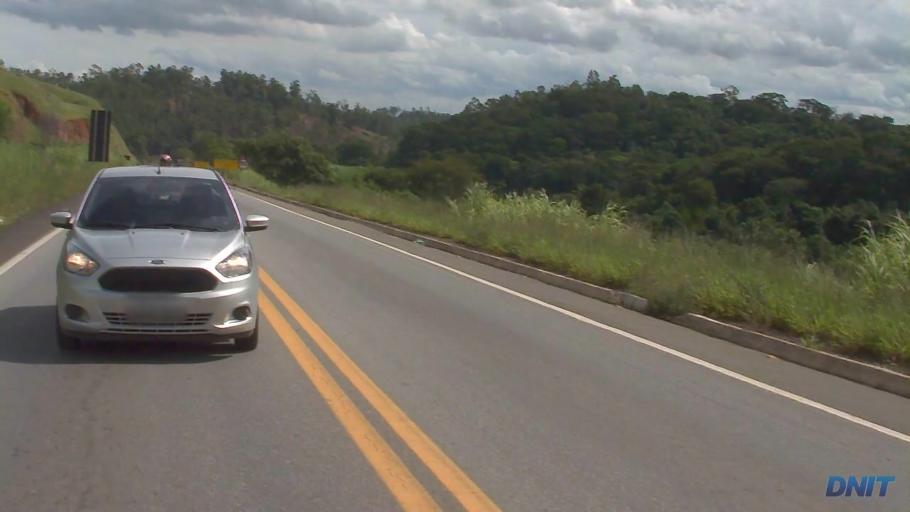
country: BR
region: Minas Gerais
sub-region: Ipatinga
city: Ipatinga
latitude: -19.4199
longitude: -42.4940
